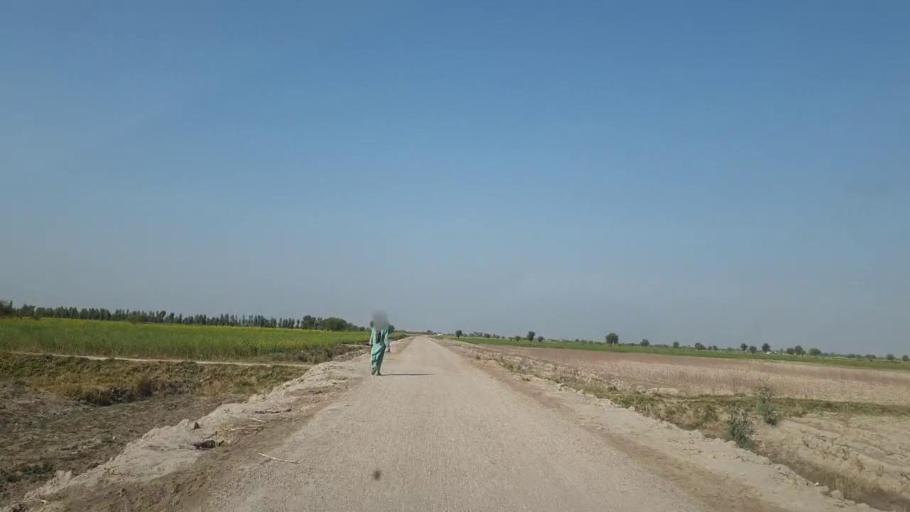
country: PK
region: Sindh
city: Mirpur Khas
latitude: 25.7284
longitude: 69.1614
